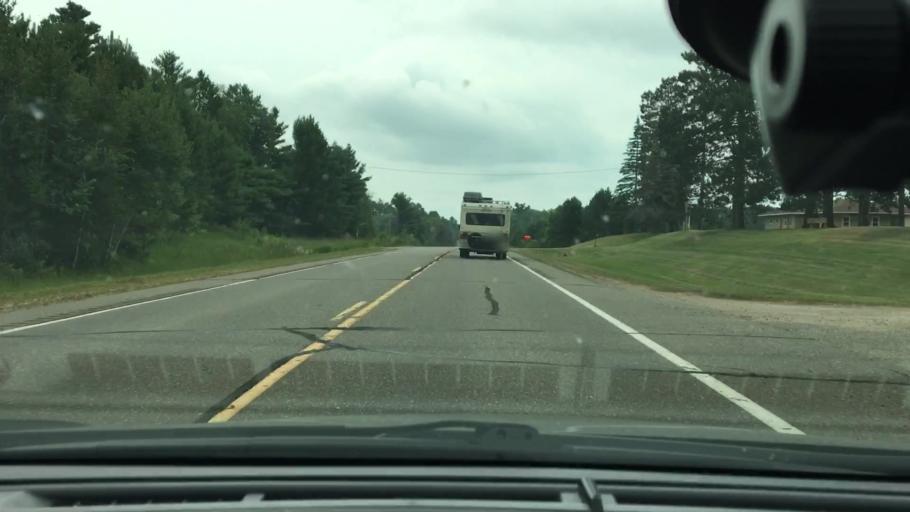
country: US
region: Minnesota
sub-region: Crow Wing County
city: Crosby
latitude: 46.4252
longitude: -93.8733
